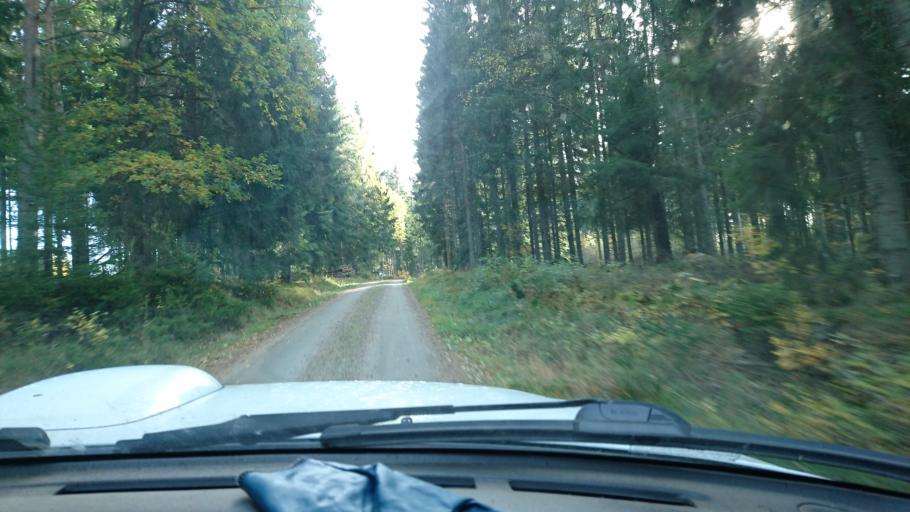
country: SE
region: Vaestra Goetaland
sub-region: Ulricehamns Kommun
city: Ulricehamn
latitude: 57.9509
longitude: 13.5307
